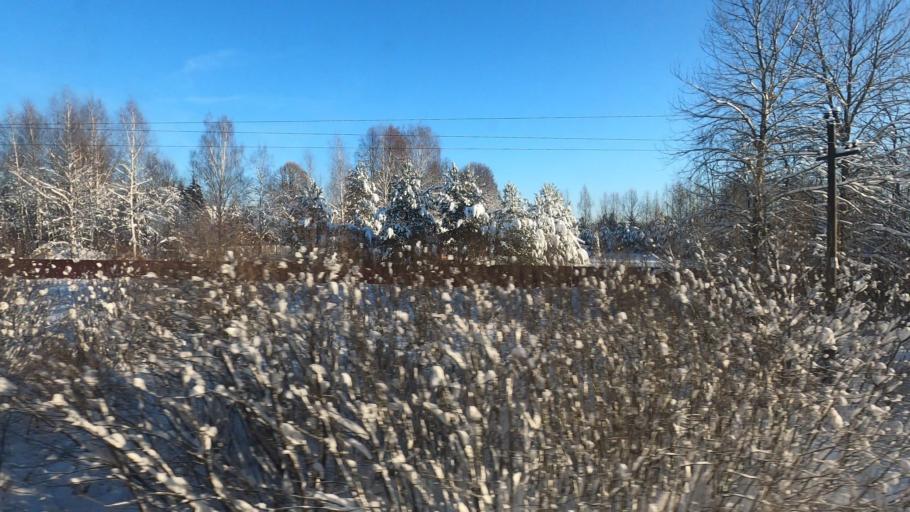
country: RU
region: Moskovskaya
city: Novo-Nikol'skoye
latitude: 56.6471
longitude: 37.5638
